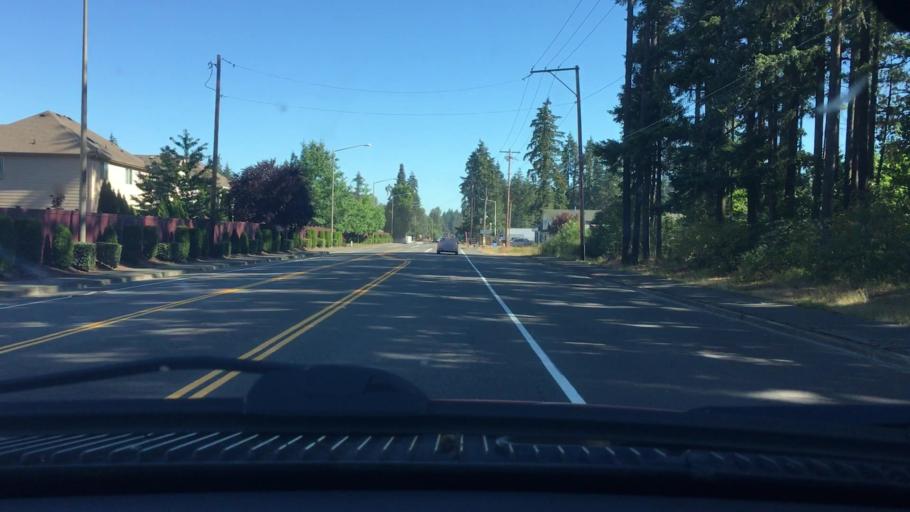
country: US
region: Washington
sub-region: King County
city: Covington
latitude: 47.3498
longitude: -122.1389
